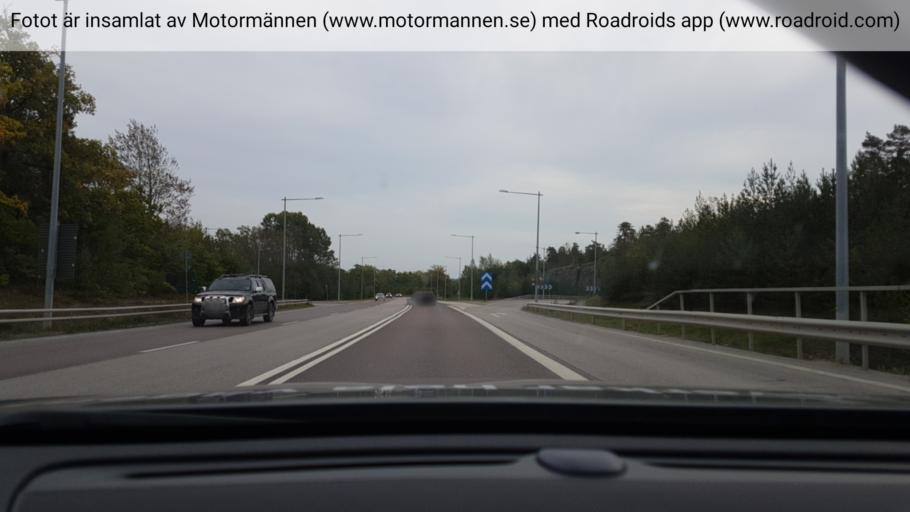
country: SE
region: Stockholm
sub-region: Nynashamns Kommun
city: Nynashamn
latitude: 58.9204
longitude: 17.9511
